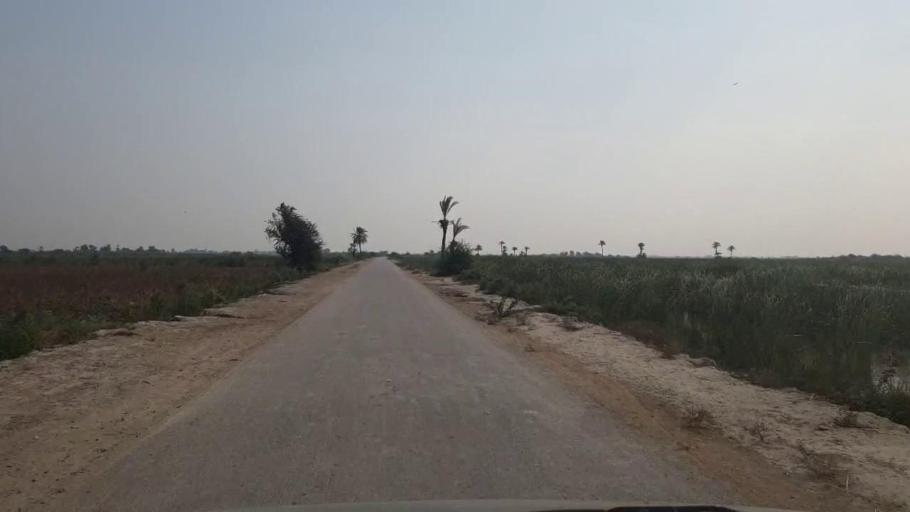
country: PK
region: Sindh
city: Tando Muhammad Khan
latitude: 25.0989
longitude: 68.3769
